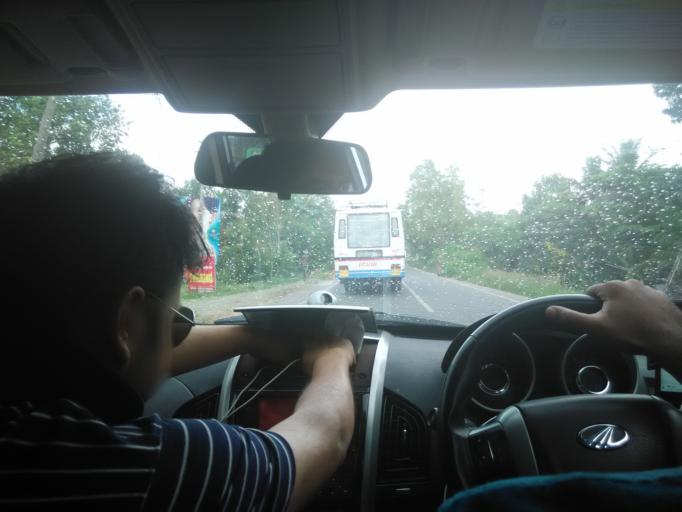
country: IN
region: Kerala
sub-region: Thiruvananthapuram
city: Attingal
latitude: 8.6495
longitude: 76.8418
